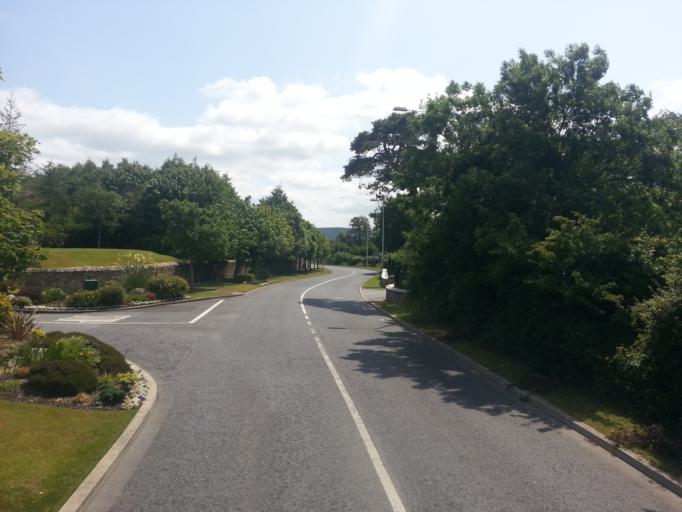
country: IE
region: Leinster
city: Sandyford
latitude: 53.2516
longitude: -6.2119
